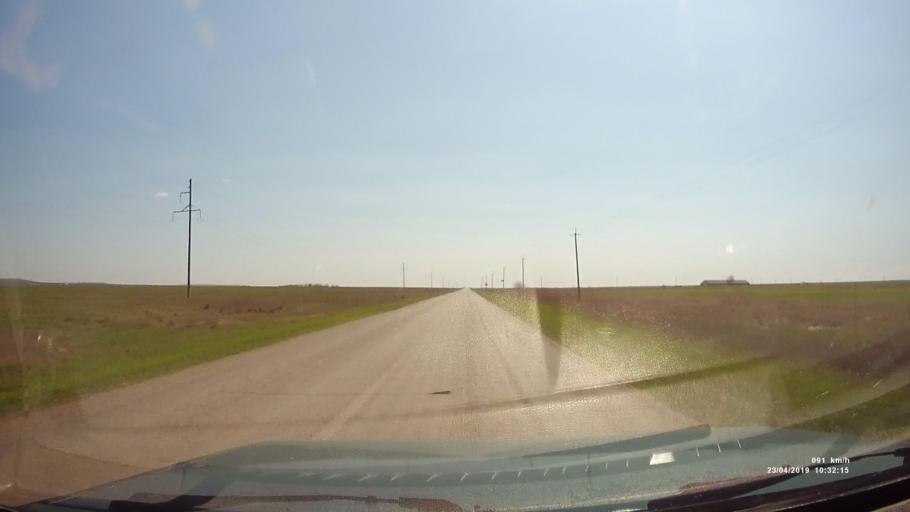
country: RU
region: Kalmykiya
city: Yashalta
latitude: 46.5813
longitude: 42.5749
